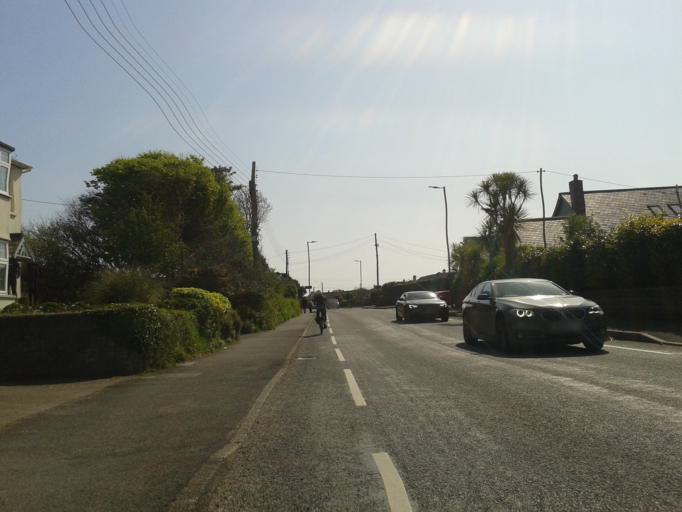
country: GB
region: England
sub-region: Devon
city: Braunton
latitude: 51.1094
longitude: -4.1715
